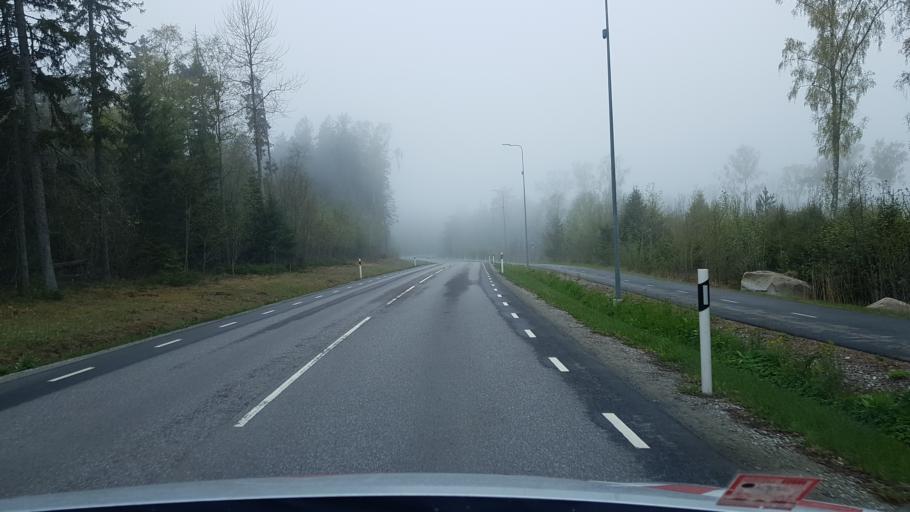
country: EE
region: Harju
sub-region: Viimsi vald
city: Viimsi
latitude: 59.5222
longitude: 24.8919
